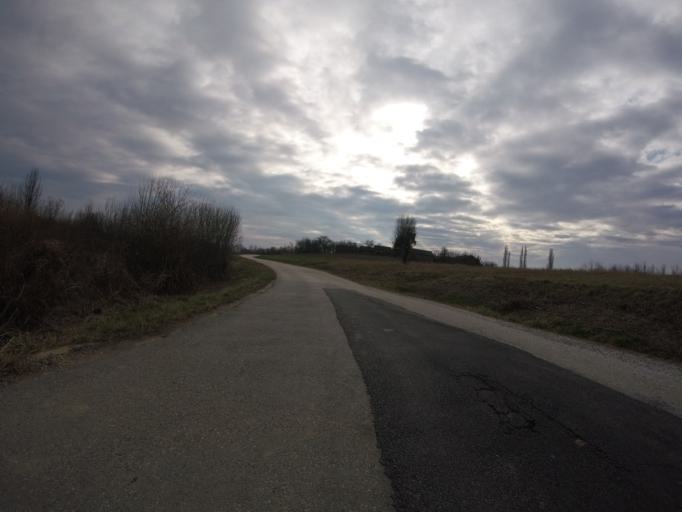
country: HR
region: Zagrebacka
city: Mraclin
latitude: 45.5155
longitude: 16.0531
